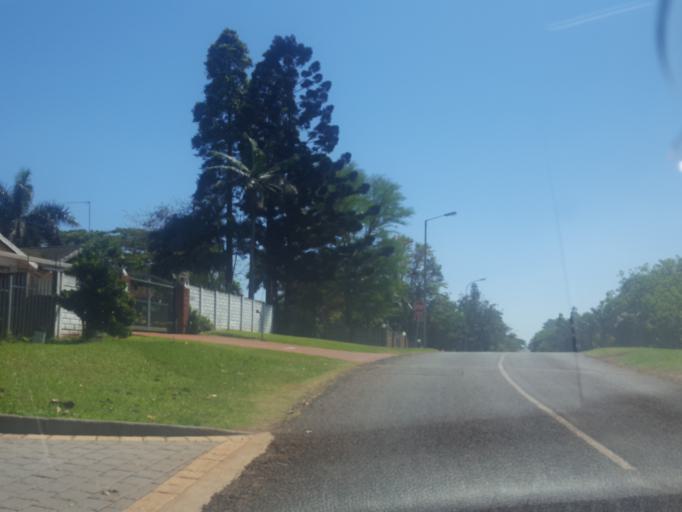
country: ZA
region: KwaZulu-Natal
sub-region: uThungulu District Municipality
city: Empangeni
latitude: -28.7524
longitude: 31.9069
